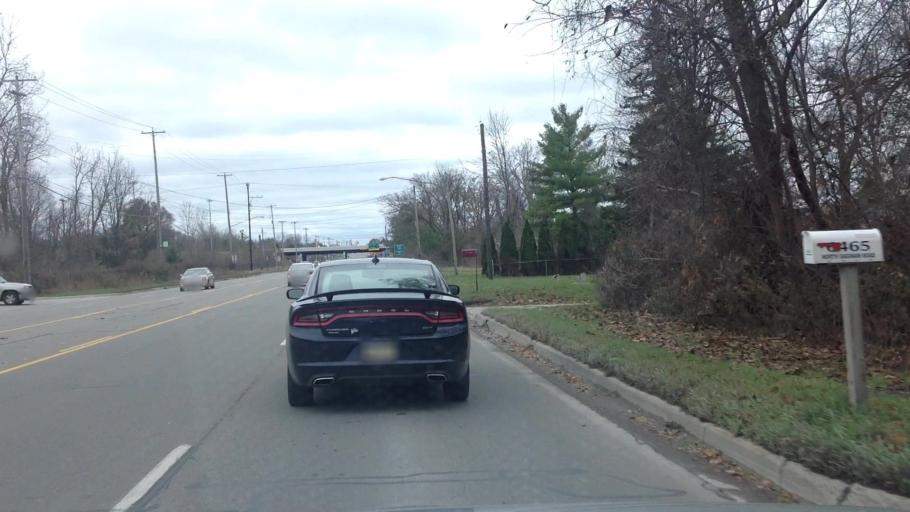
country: US
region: Michigan
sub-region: Genesee County
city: Beecher
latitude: 43.1030
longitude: -83.6944
